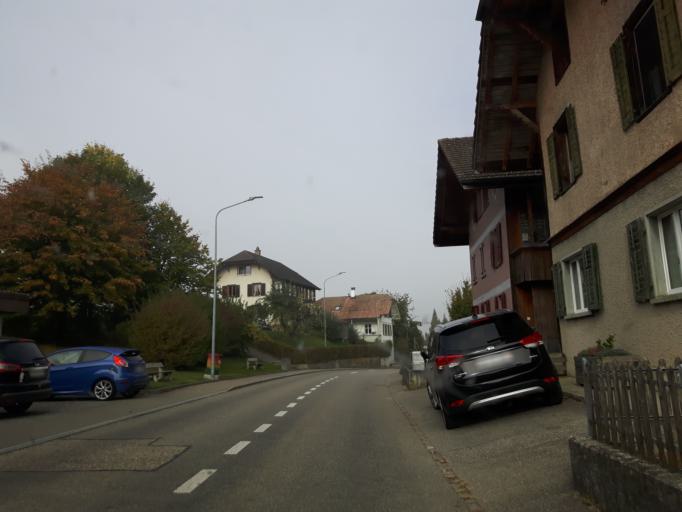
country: CH
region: Bern
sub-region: Oberaargau
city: Roggwil
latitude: 47.2371
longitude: 7.8244
